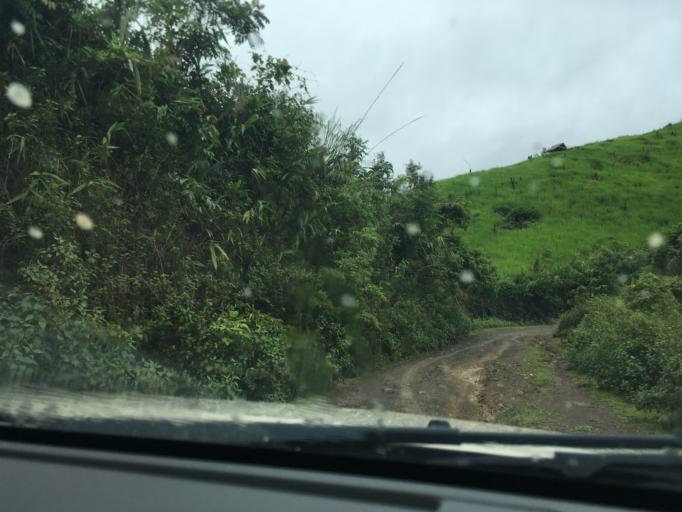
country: LA
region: Phongsali
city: Phongsali
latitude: 21.3565
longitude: 102.1169
